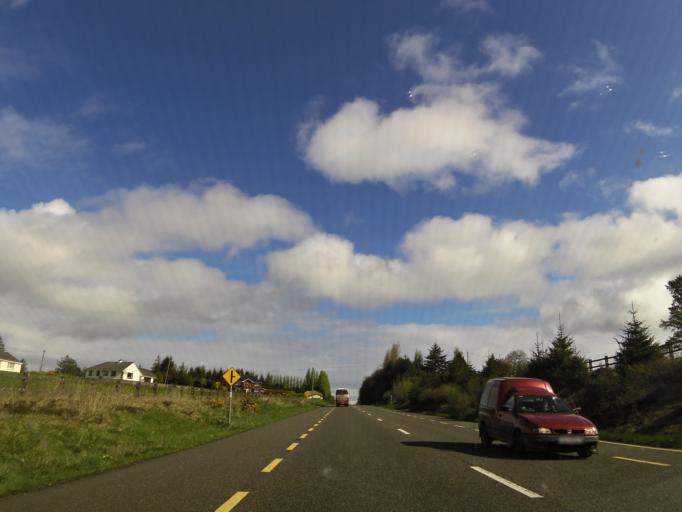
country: IE
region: Connaught
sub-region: Maigh Eo
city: Ballyhaunis
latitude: 53.8891
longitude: -8.8015
